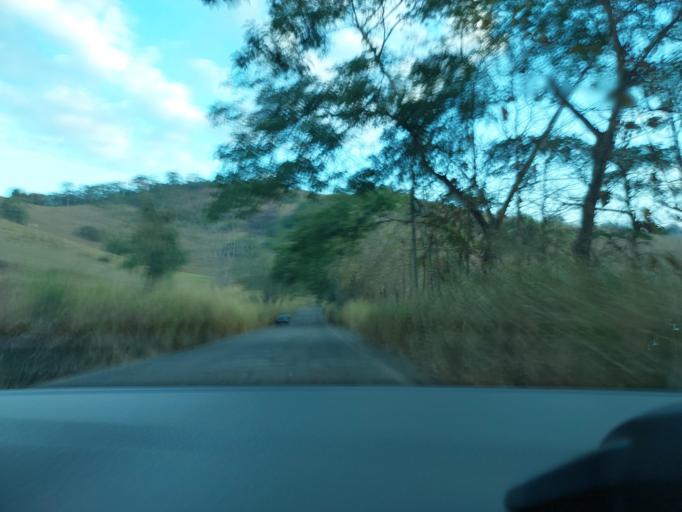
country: BR
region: Rio de Janeiro
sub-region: Natividade
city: Natividade
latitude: -21.1967
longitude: -42.1169
